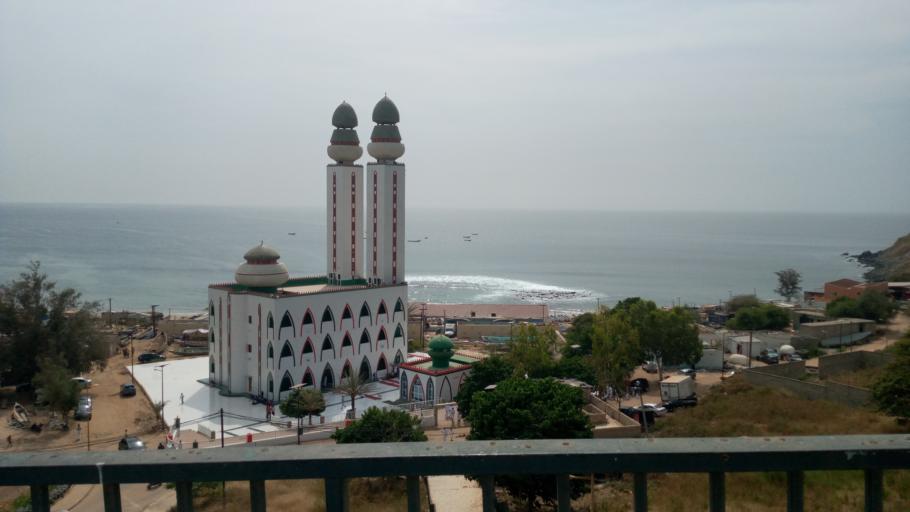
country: SN
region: Dakar
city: Mermoz Boabab
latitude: 14.7167
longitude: -17.4900
